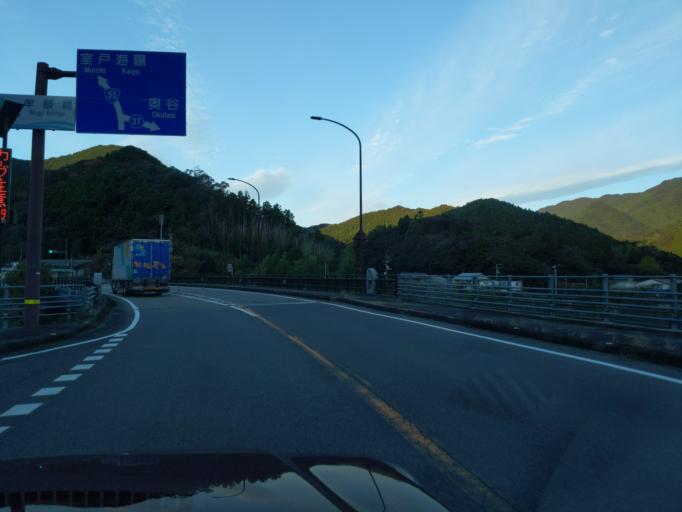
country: JP
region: Tokushima
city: Anan
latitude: 33.6872
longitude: 134.4220
